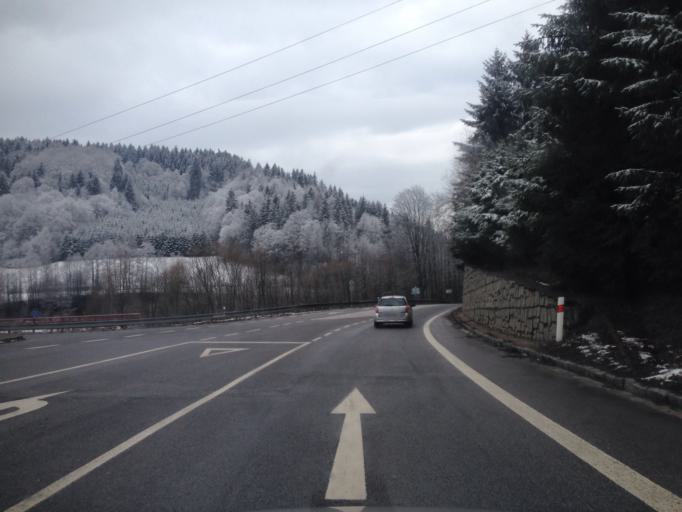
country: CZ
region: Liberecky
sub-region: Okres Semily
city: Ponikla
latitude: 50.6318
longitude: 15.4645
